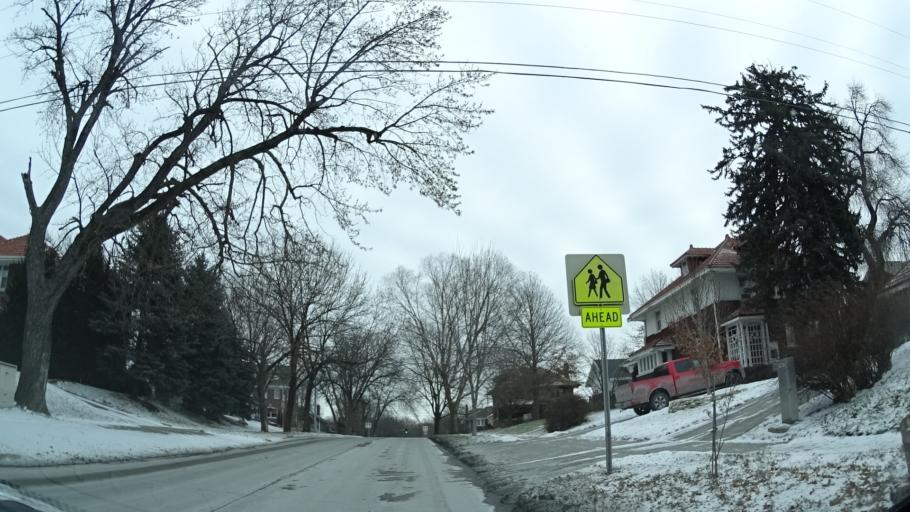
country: US
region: Nebraska
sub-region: Douglas County
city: Omaha
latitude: 41.2579
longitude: -95.9948
